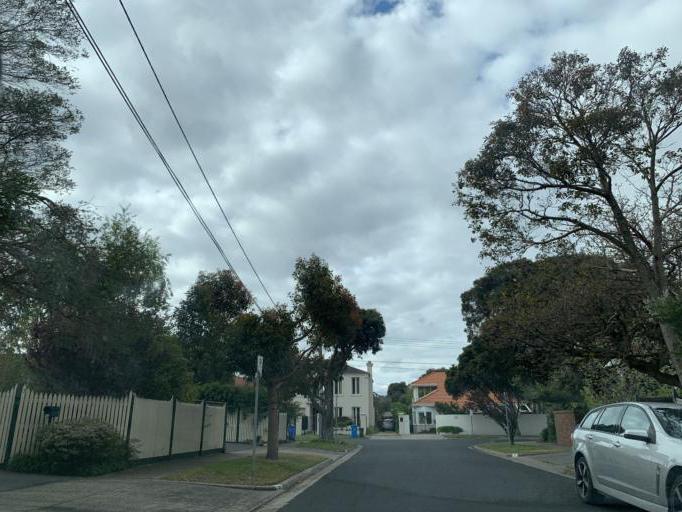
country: AU
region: Victoria
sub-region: Bayside
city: Black Rock
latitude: -37.9693
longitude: 145.0199
